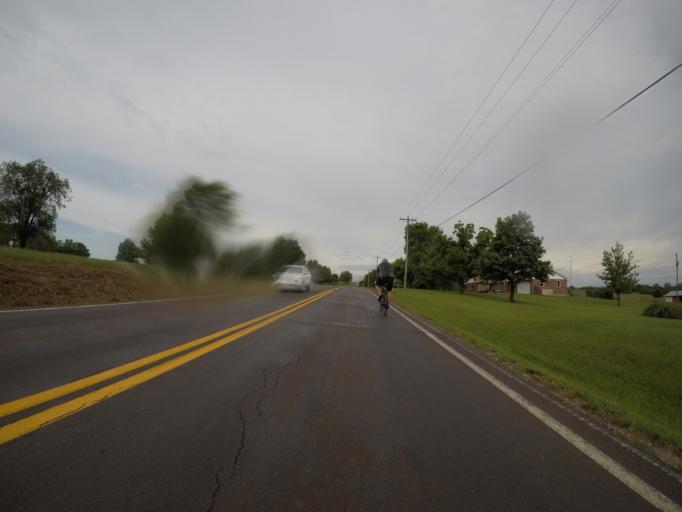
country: US
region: Kansas
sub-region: Shawnee County
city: Auburn
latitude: 38.9563
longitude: -95.7813
